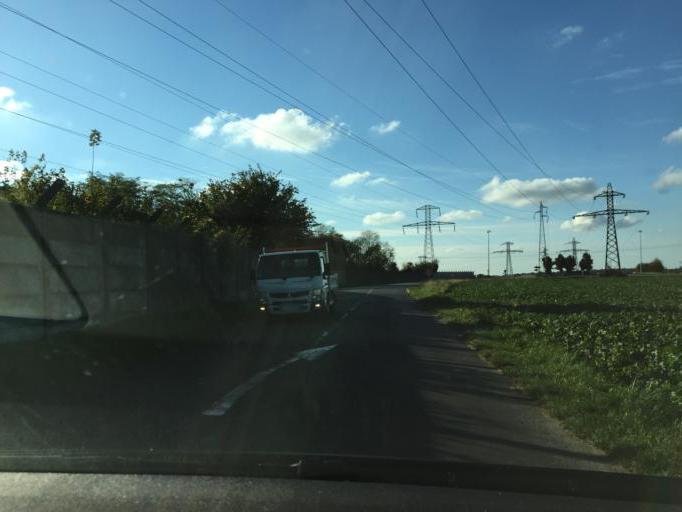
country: FR
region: Ile-de-France
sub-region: Departement des Yvelines
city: Jouy-en-Josas
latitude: 48.7498
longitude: 2.1695
